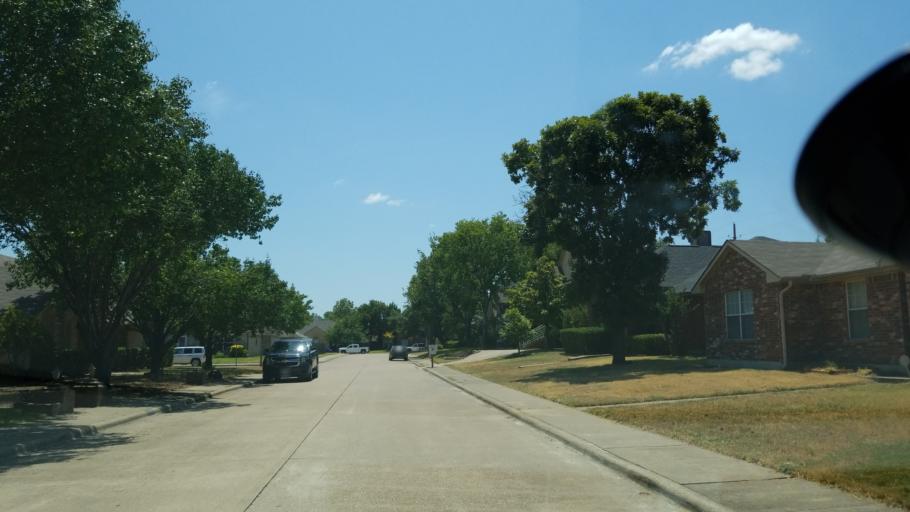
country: US
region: Texas
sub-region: Dallas County
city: Duncanville
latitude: 32.6387
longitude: -96.8858
